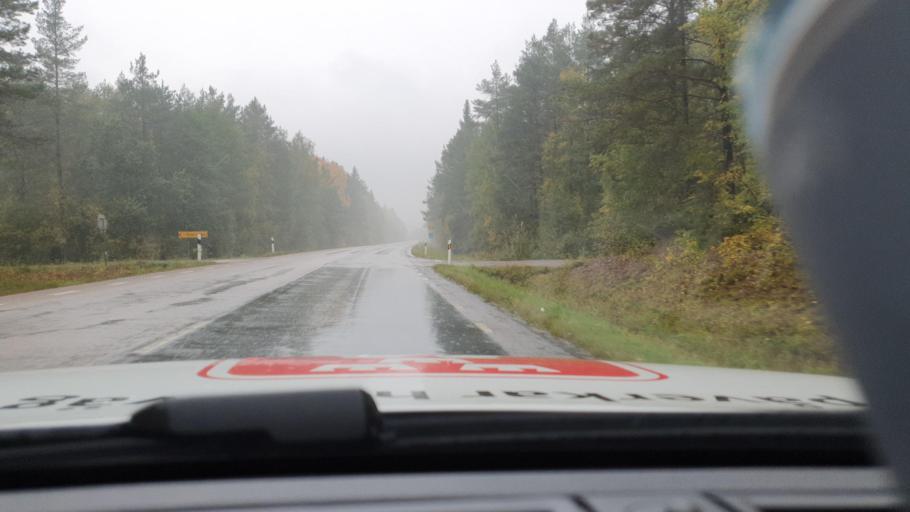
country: SE
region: Uppsala
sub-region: Tierps Kommun
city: Orbyhus
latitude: 60.2230
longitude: 17.6846
